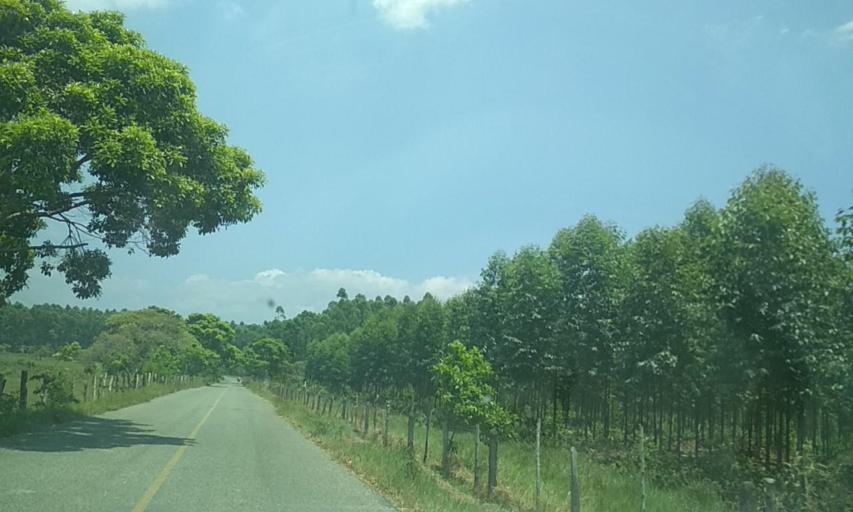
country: MX
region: Tabasco
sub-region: Huimanguillo
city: Francisco Rueda
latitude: 17.8382
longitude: -93.9076
